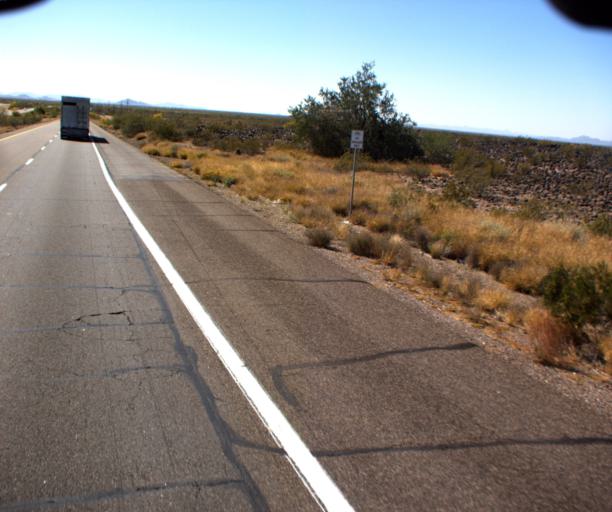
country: US
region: Arizona
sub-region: Maricopa County
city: Gila Bend
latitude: 32.8523
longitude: -113.2590
